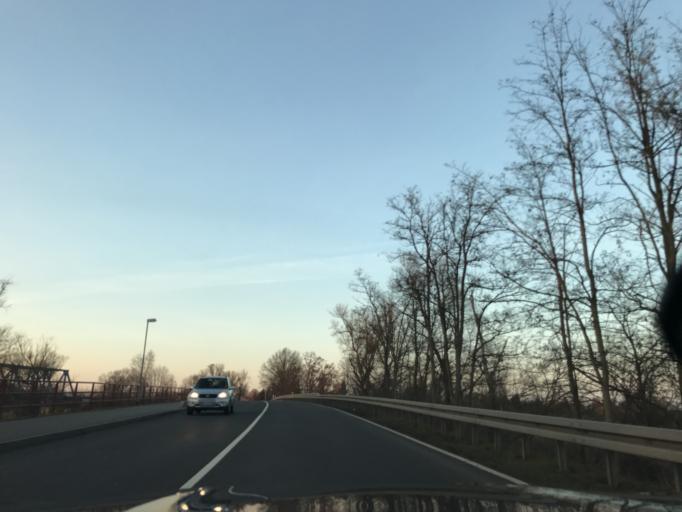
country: DE
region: Brandenburg
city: Brandenburg an der Havel
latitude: 52.4905
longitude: 12.4611
